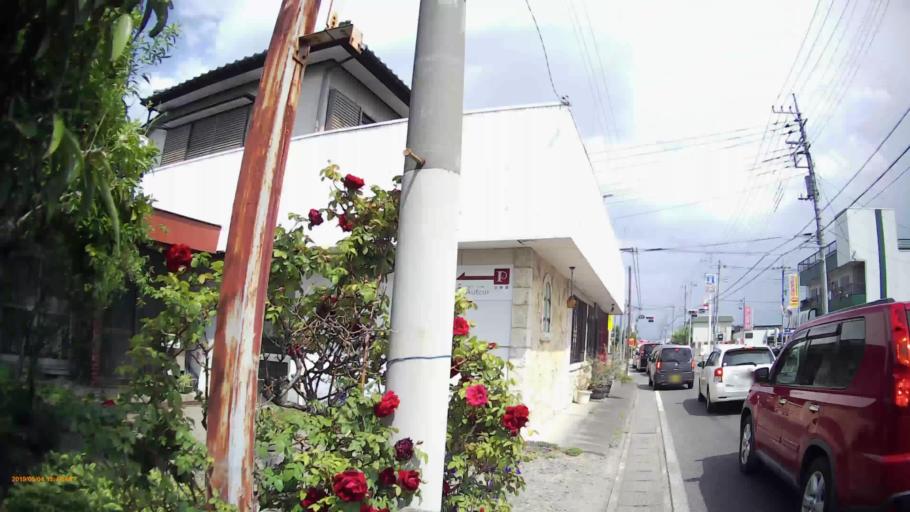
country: JP
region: Yamanashi
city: Ryuo
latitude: 35.6641
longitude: 138.5257
